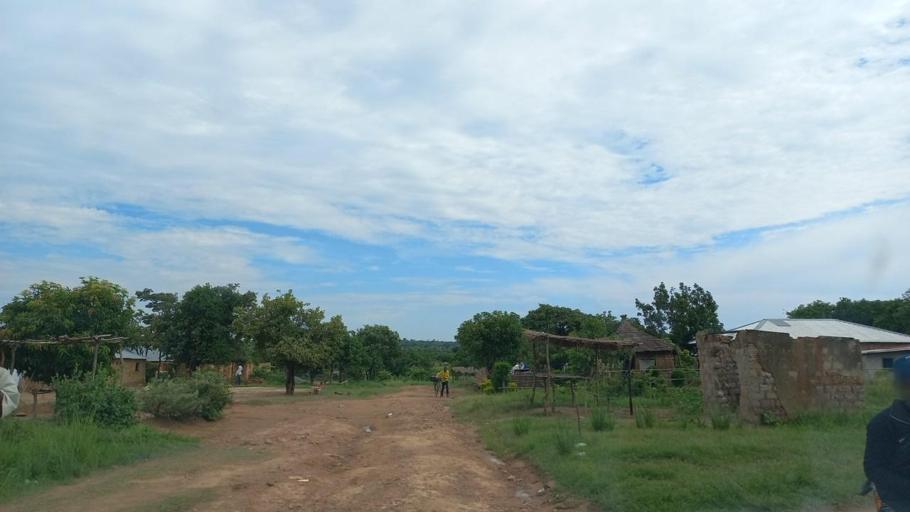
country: ZM
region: Copperbelt
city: Kitwe
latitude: -12.8677
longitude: 28.3349
